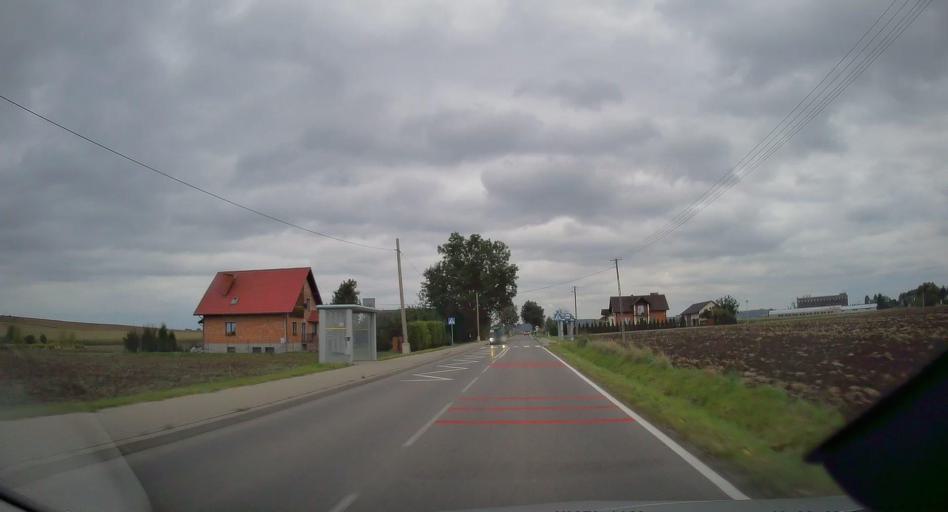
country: PL
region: Lesser Poland Voivodeship
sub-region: Powiat krakowski
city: Slomniki
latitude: 50.2121
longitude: 20.0857
